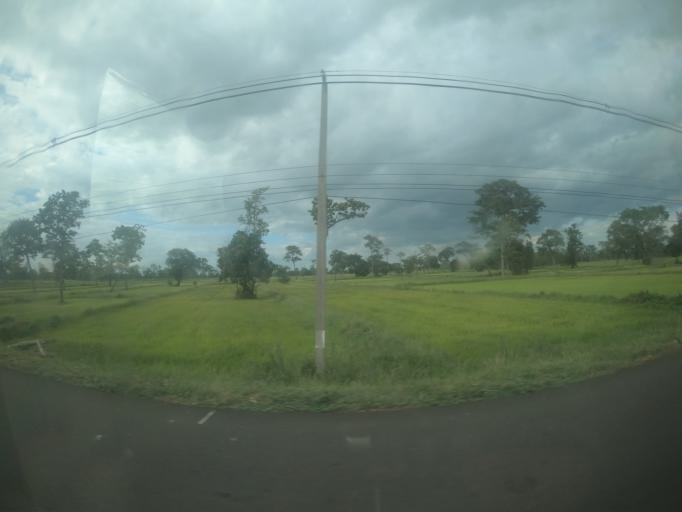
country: TH
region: Surin
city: Kap Choeng
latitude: 14.5400
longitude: 103.5210
